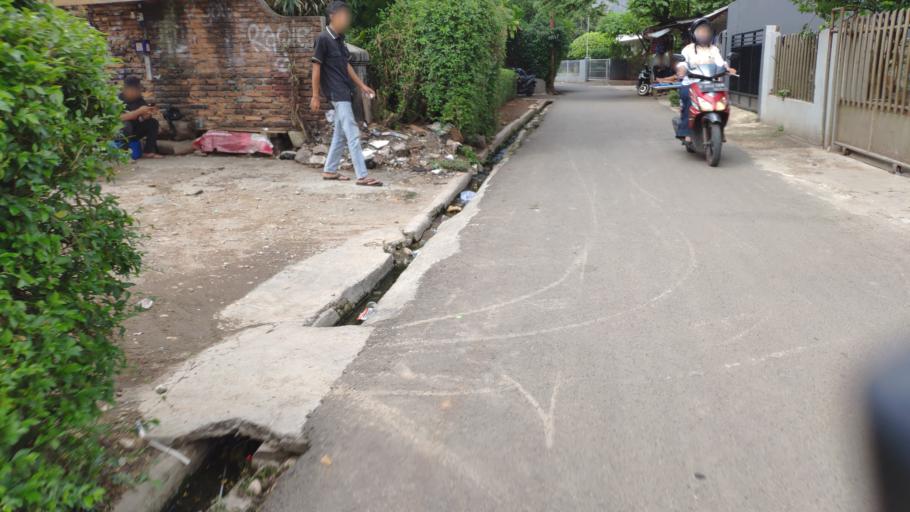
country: ID
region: West Java
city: Depok
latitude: -6.3210
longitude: 106.8263
